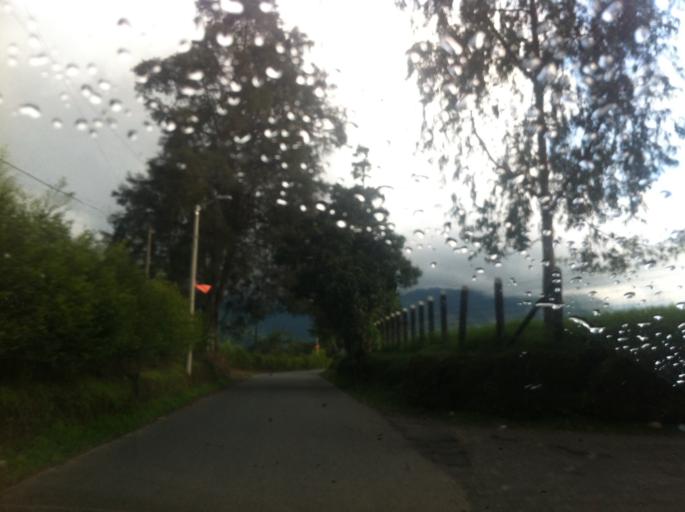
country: CO
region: Quindio
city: Circasia
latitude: 4.5876
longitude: -75.6333
